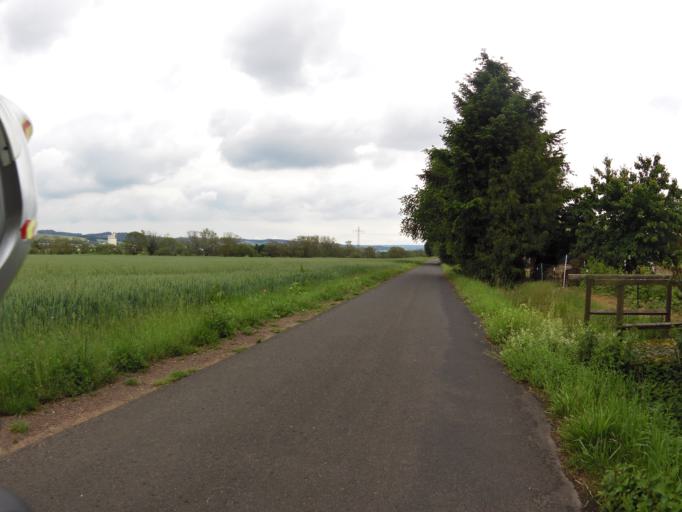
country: DE
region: Hesse
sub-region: Regierungsbezirk Kassel
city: Rotenburg an der Fulda
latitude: 50.9836
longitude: 9.7559
